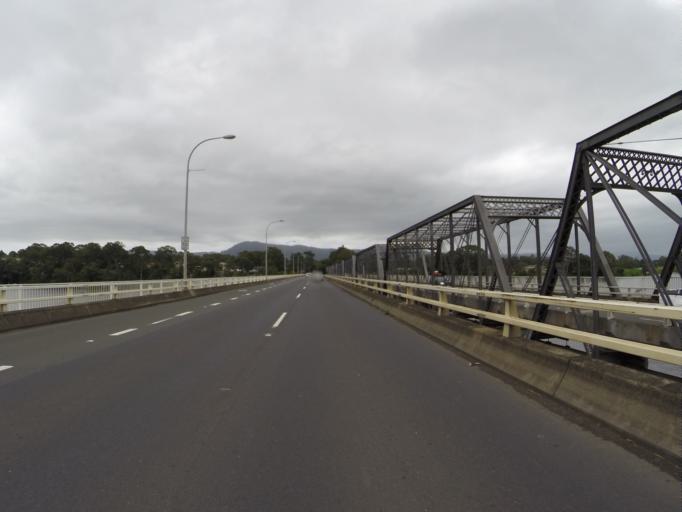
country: AU
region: New South Wales
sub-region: Shoalhaven Shire
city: Bomaderry
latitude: -34.8652
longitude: 150.6017
